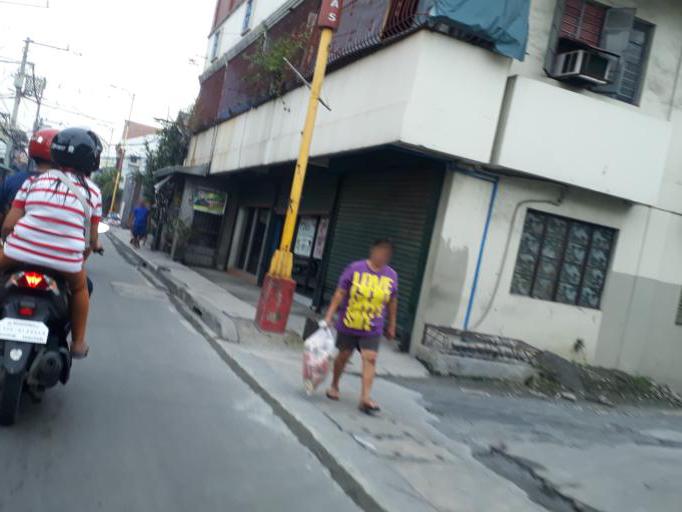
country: PH
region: Calabarzon
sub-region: Province of Rizal
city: Navotas
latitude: 14.6598
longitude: 120.9449
